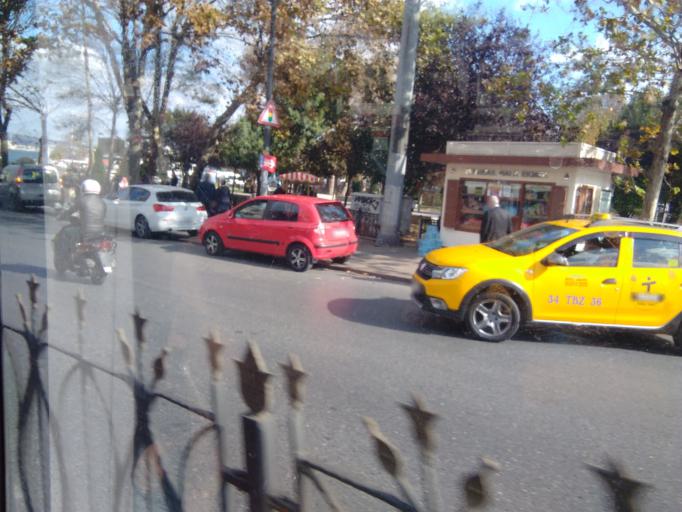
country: TR
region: Istanbul
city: Eminoenue
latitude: 41.0156
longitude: 28.9763
